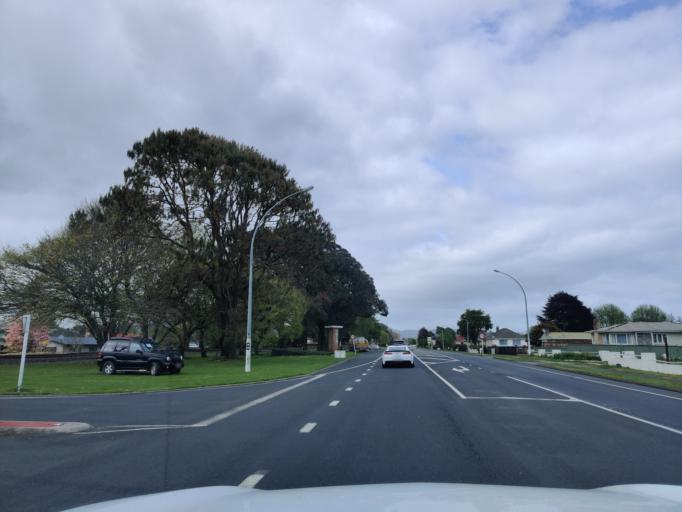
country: NZ
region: Waikato
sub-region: Waikato District
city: Ngaruawahia
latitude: -37.5388
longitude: 175.1585
